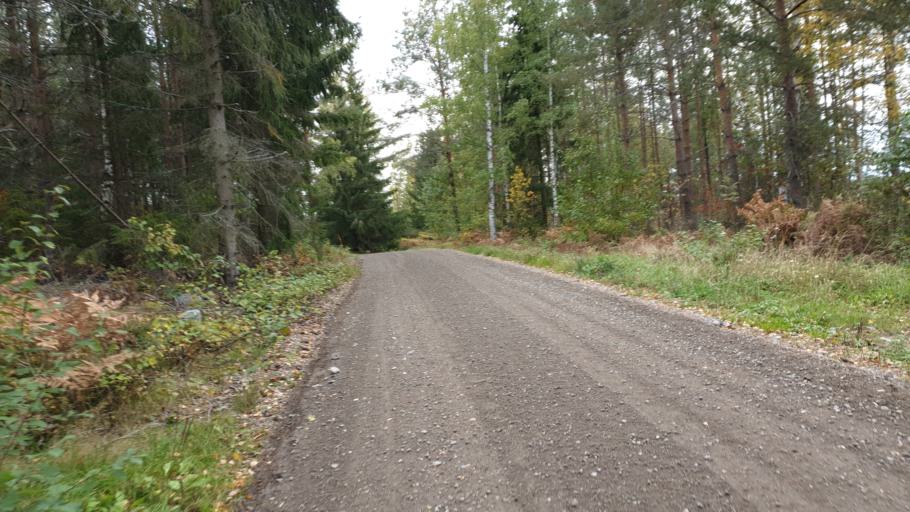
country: SE
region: Vaestmanland
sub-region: Sala Kommun
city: Sala
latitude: 59.8156
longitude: 16.6582
